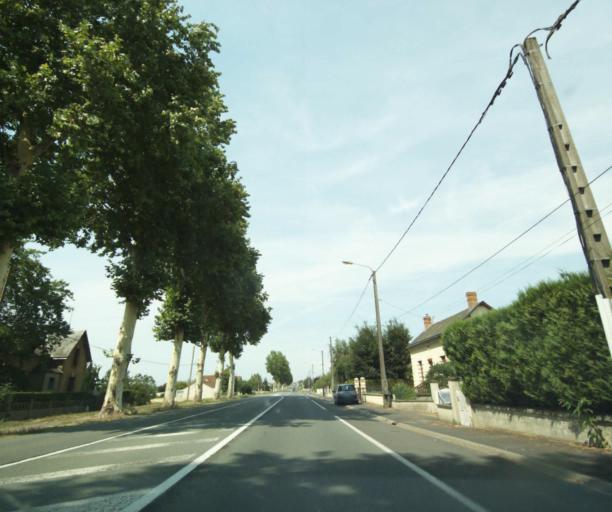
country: FR
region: Centre
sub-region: Departement d'Indre-et-Loire
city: La Celle-Saint-Avant
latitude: 47.0120
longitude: 0.6017
